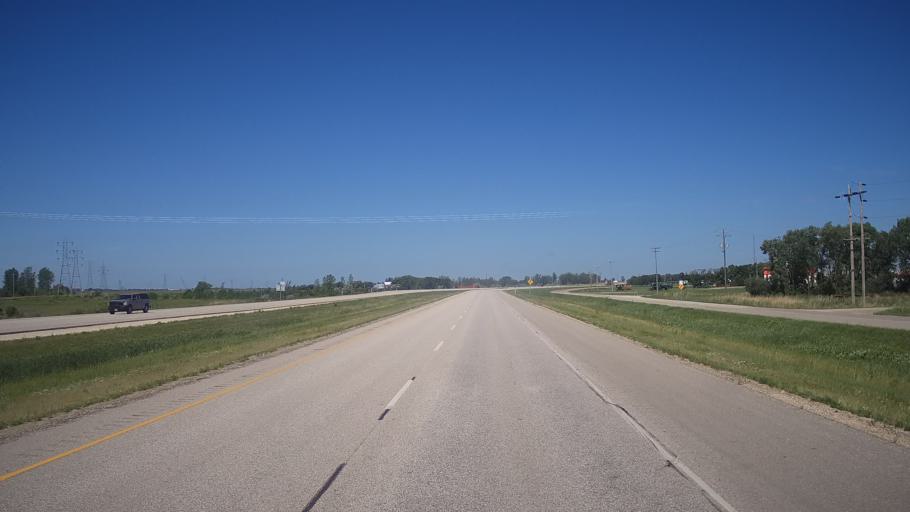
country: CA
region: Manitoba
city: Portage la Prairie
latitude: 49.9606
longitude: -98.3461
